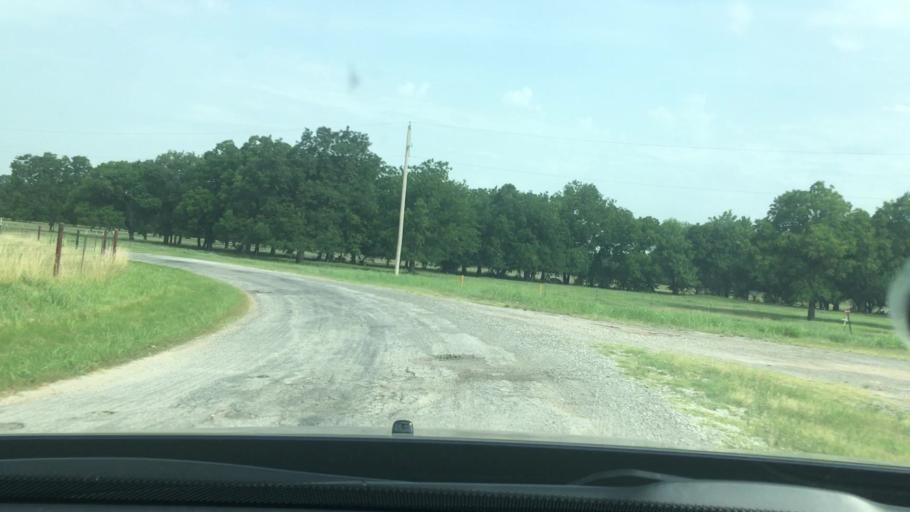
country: US
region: Oklahoma
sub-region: Garvin County
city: Pauls Valley
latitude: 34.8253
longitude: -97.1957
